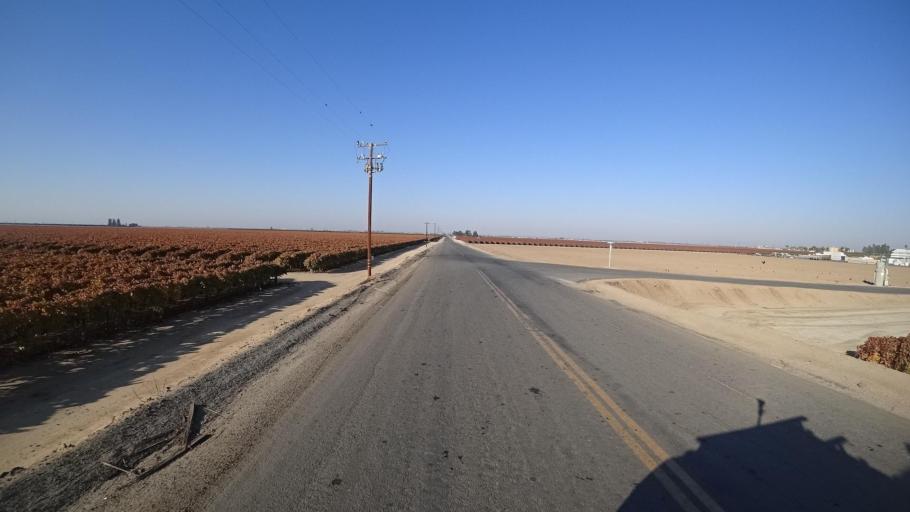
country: US
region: California
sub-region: Kern County
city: Delano
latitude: 35.7687
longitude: -119.1783
